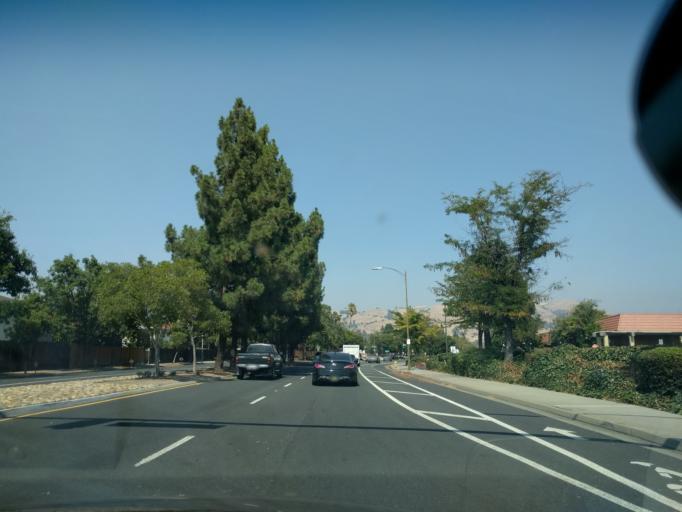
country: US
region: California
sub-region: Santa Clara County
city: Alum Rock
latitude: 37.3880
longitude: -121.8590
